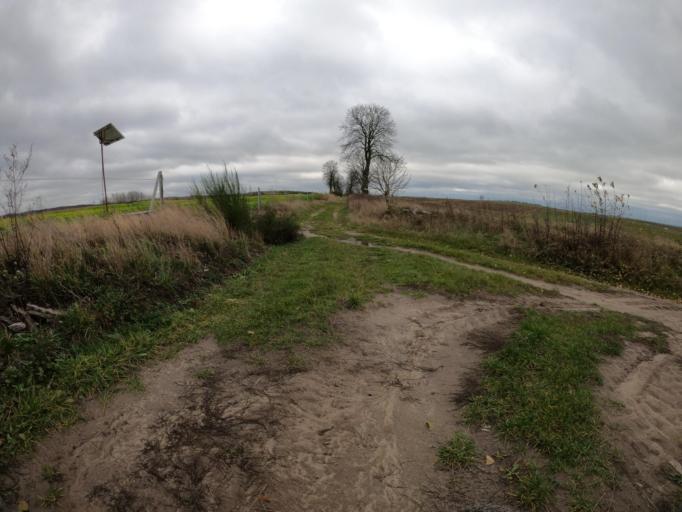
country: PL
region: West Pomeranian Voivodeship
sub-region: Powiat walecki
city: Tuczno
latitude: 53.2493
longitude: 16.2042
